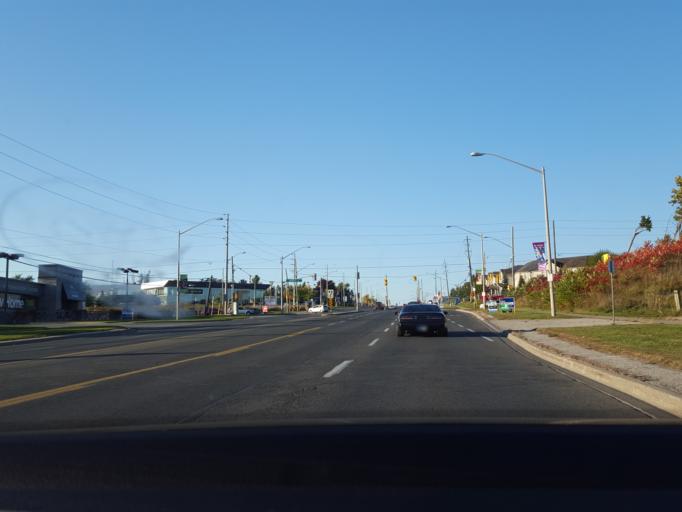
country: CA
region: Ontario
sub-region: York
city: Richmond Hill
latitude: 43.9067
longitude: -79.4454
